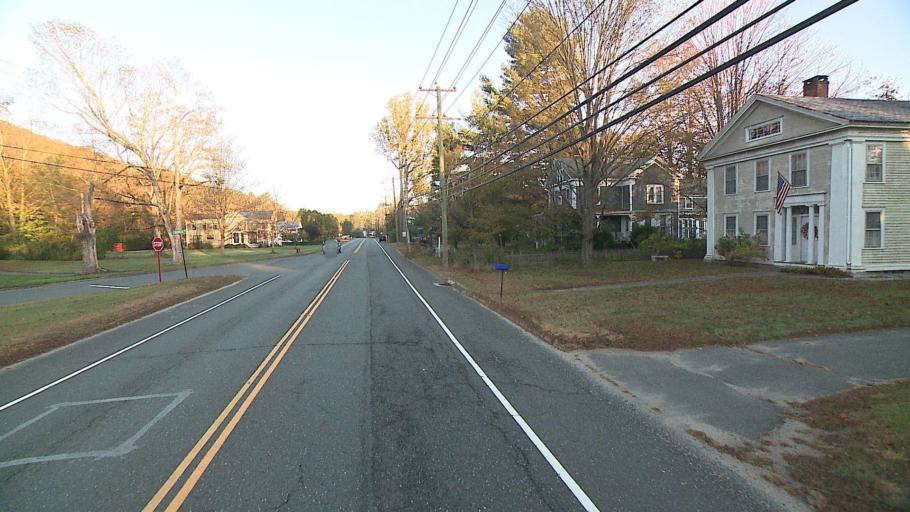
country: US
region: Connecticut
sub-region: Litchfield County
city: New Hartford Center
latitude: 41.8751
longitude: -72.9674
